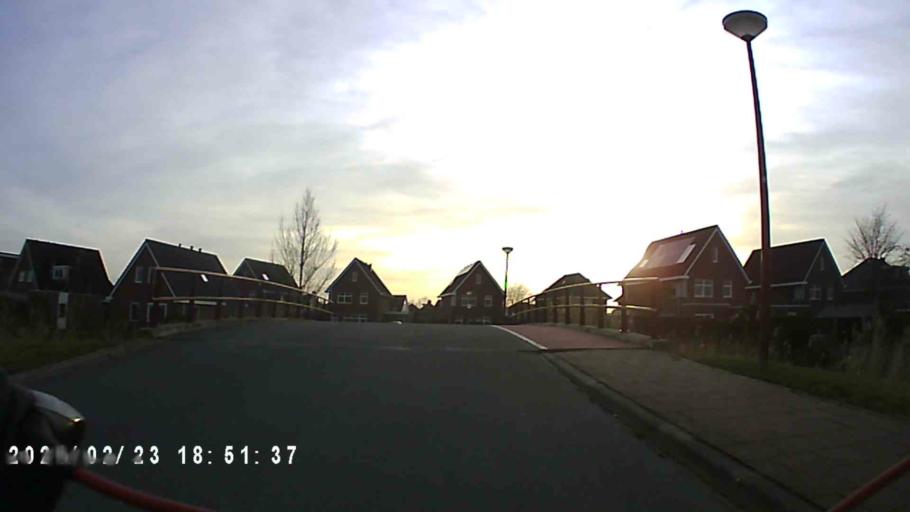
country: NL
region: Groningen
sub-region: Gemeente Winsum
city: Winsum
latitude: 53.3366
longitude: 6.5316
